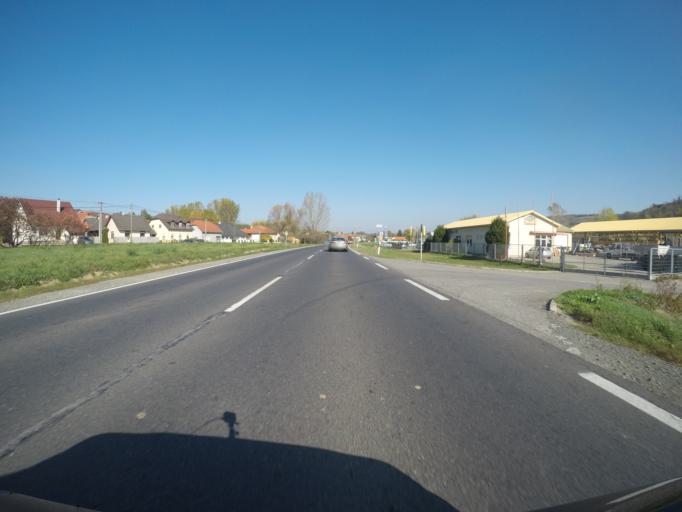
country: HU
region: Tolna
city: Szentgalpuszta
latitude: 46.3419
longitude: 18.5886
